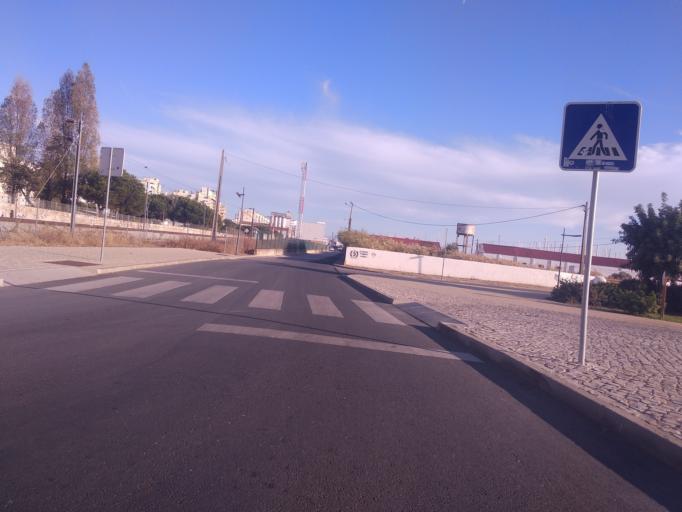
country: PT
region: Faro
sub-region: Faro
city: Faro
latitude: 37.0240
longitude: -7.9448
